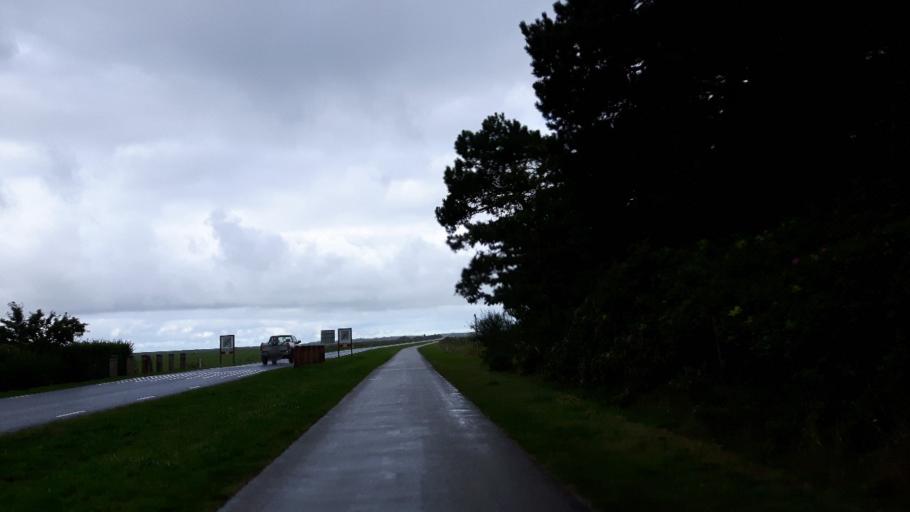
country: NL
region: Friesland
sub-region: Gemeente Ameland
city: Nes
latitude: 53.4460
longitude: 5.7631
